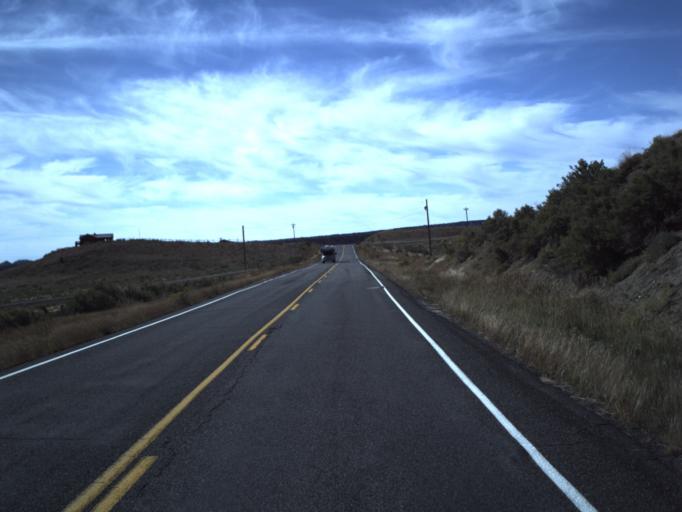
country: US
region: Utah
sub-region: Garfield County
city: Panguitch
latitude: 37.6460
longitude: -112.0806
